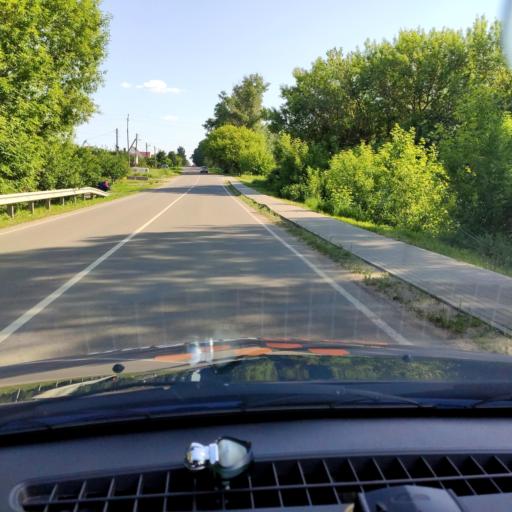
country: RU
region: Voronezj
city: Podgornoye
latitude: 51.8852
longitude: 39.1725
